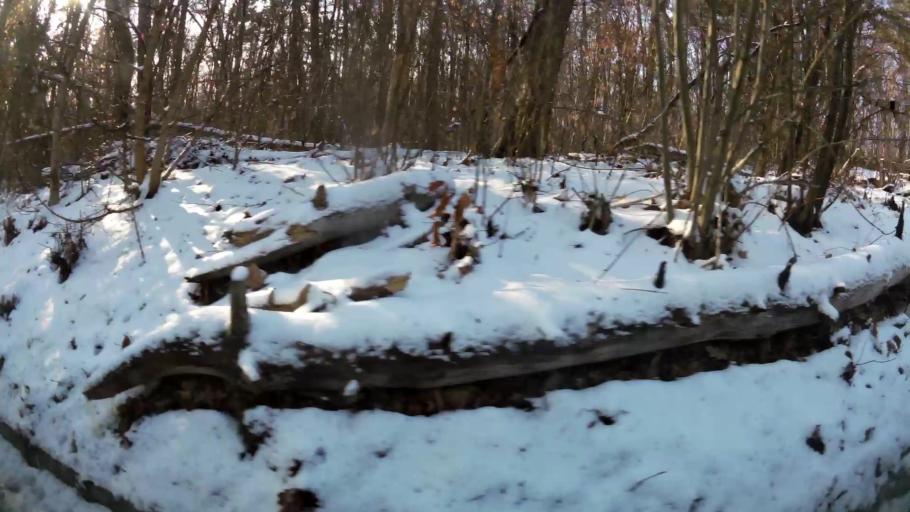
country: BG
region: Sofia-Capital
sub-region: Stolichna Obshtina
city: Sofia
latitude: 42.6699
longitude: 23.3439
